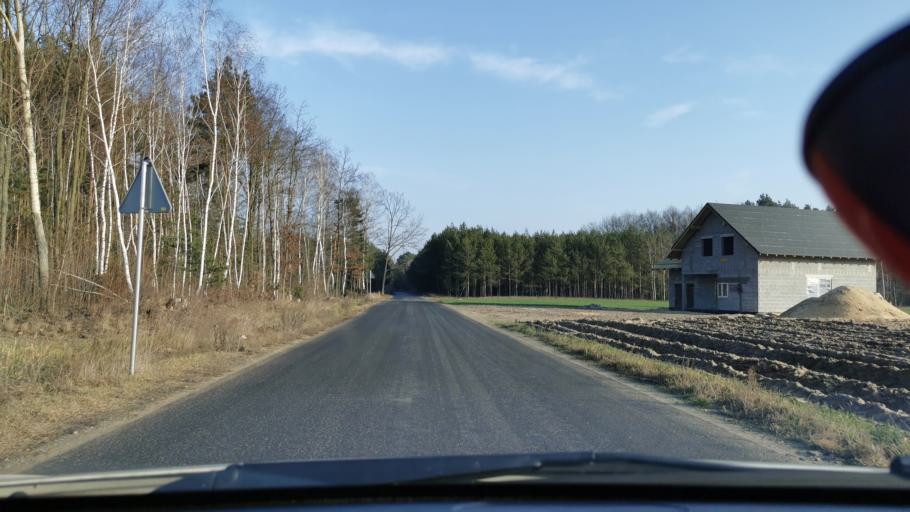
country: PL
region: Greater Poland Voivodeship
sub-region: Powiat kaliski
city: Opatowek
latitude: 51.6602
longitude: 18.2579
